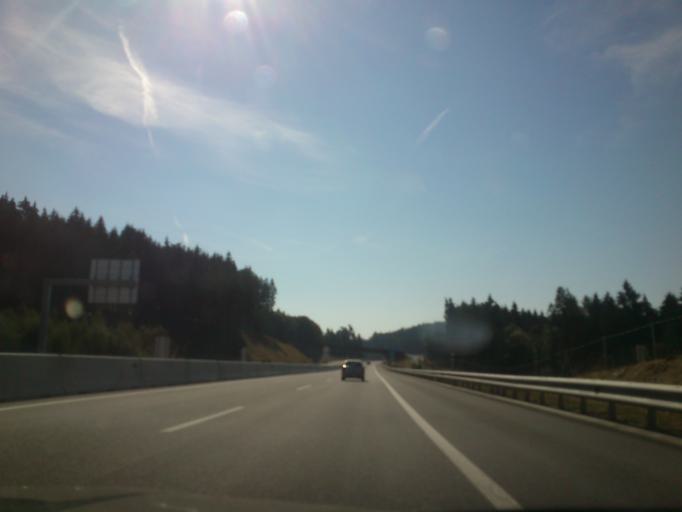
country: AT
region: Upper Austria
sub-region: Politischer Bezirk Freistadt
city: Freistadt
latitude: 48.5233
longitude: 14.5080
